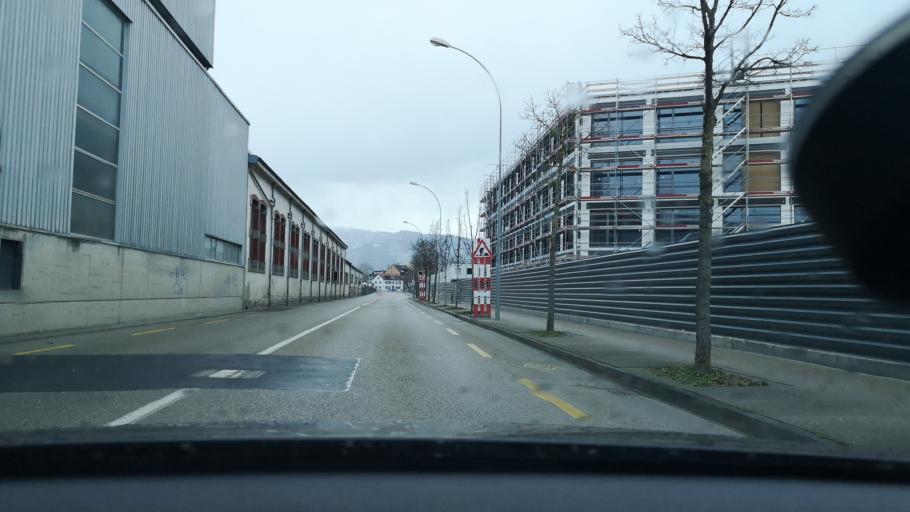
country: CH
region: Vaud
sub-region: Jura-Nord vaudois District
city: Yverdon-les-Bains
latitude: 46.7843
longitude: 6.6419
